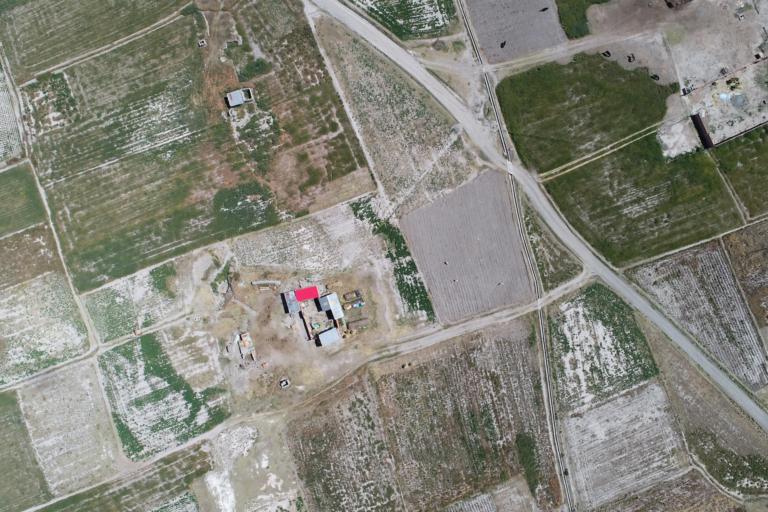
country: BO
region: La Paz
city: Achacachi
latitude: -16.0134
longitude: -68.7222
